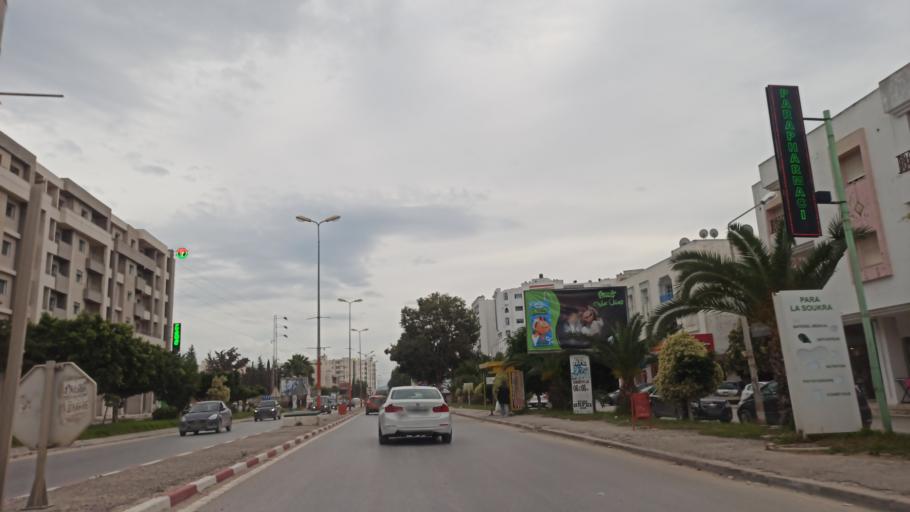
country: TN
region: Ariana
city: Ariana
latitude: 36.8631
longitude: 10.2535
